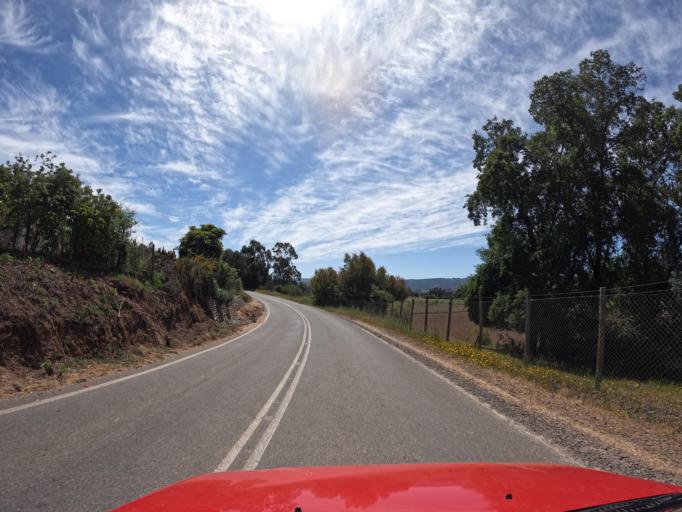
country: CL
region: Maule
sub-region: Provincia de Talca
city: Talca
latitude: -35.0059
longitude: -71.7893
